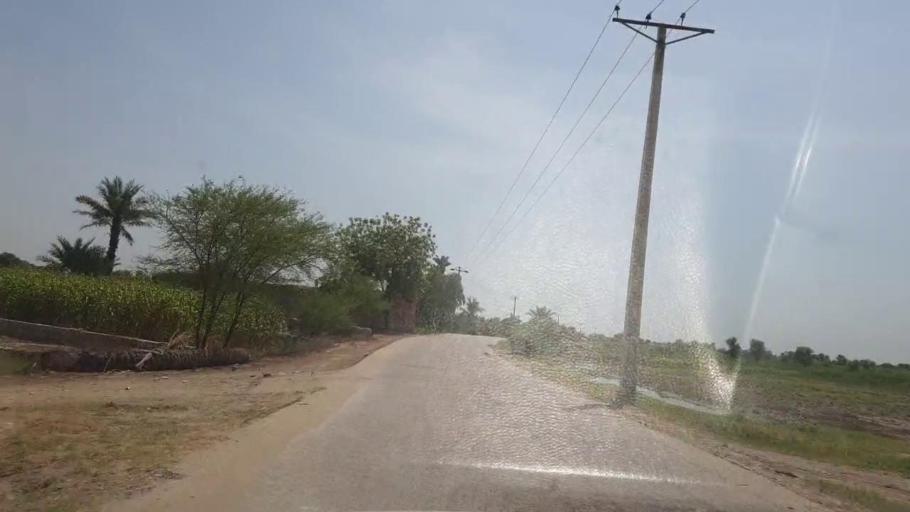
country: PK
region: Sindh
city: Bozdar
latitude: 27.0693
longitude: 68.5941
